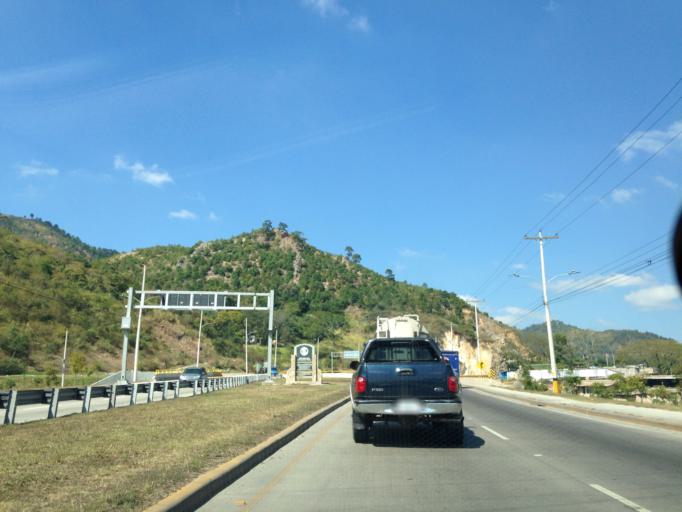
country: HN
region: Francisco Morazan
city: El Lolo
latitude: 14.1175
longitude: -87.2537
